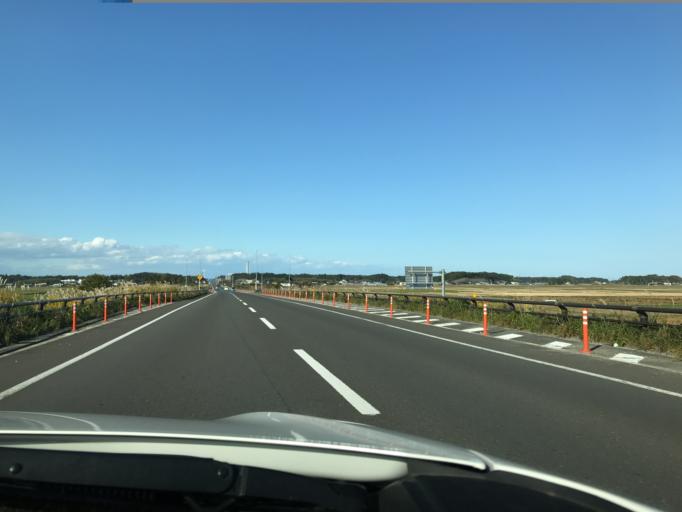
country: JP
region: Miyagi
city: Marumori
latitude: 37.7912
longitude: 140.9440
